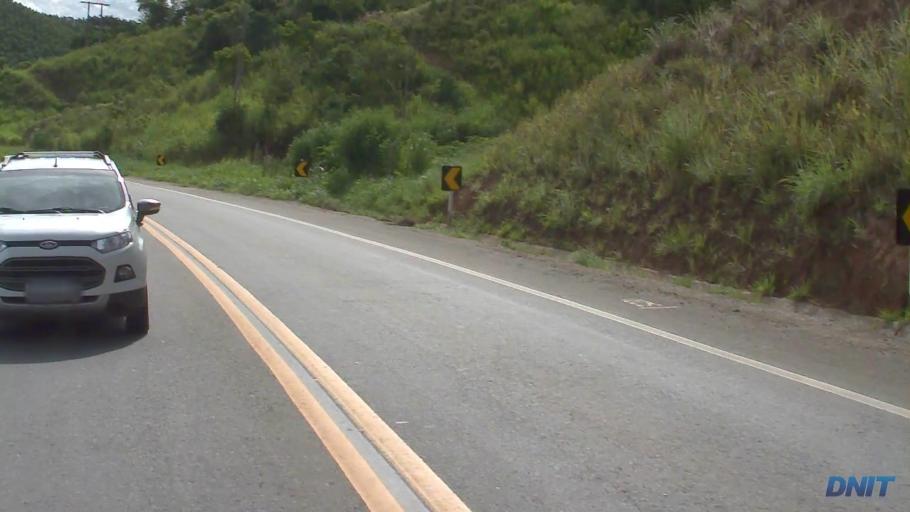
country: BR
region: Minas Gerais
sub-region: Belo Oriente
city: Belo Oriente
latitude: -19.2678
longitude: -42.3545
